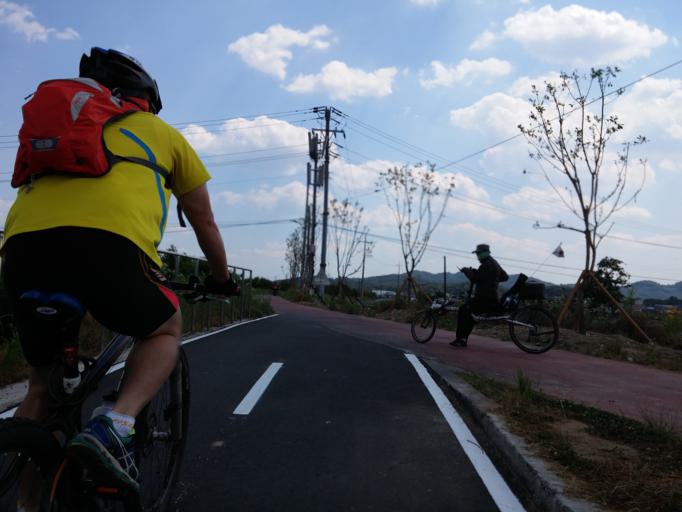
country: KR
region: Chungcheongbuk-do
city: Cheongju-si
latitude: 36.5955
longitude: 127.4971
